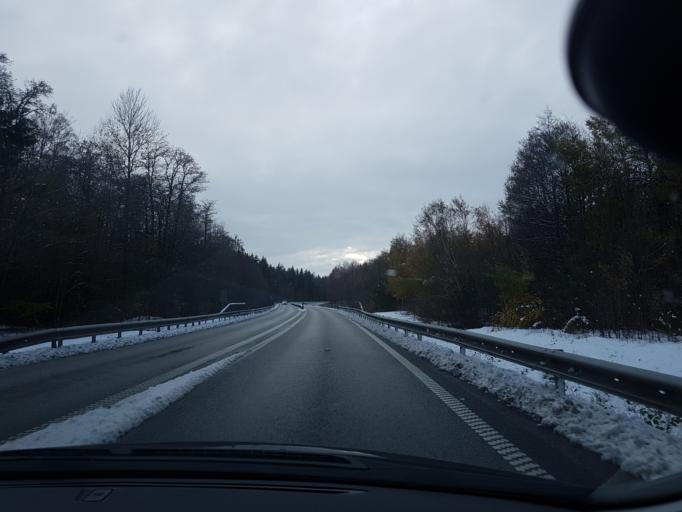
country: SE
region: Joenkoeping
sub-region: Vetlanda Kommun
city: Vetlanda
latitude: 57.4173
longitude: 15.1047
